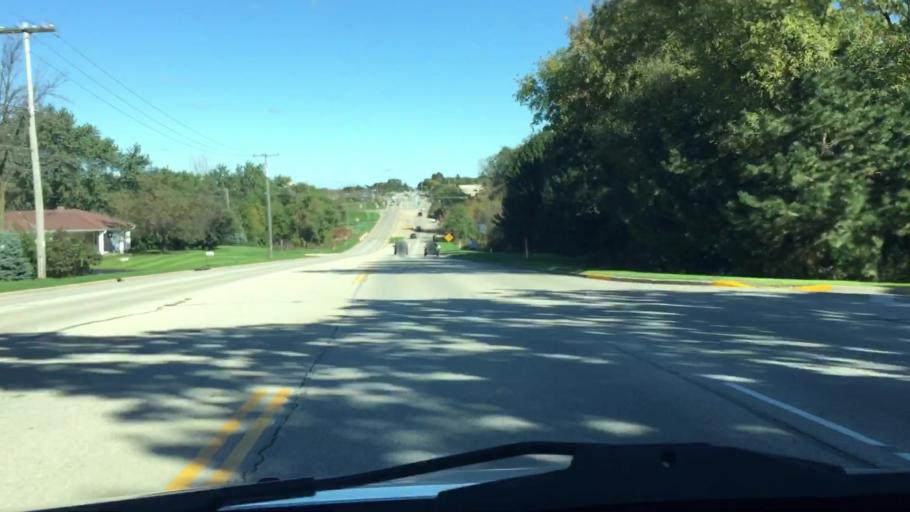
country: US
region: Wisconsin
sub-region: Waukesha County
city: Waukesha
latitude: 43.0437
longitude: -88.2257
